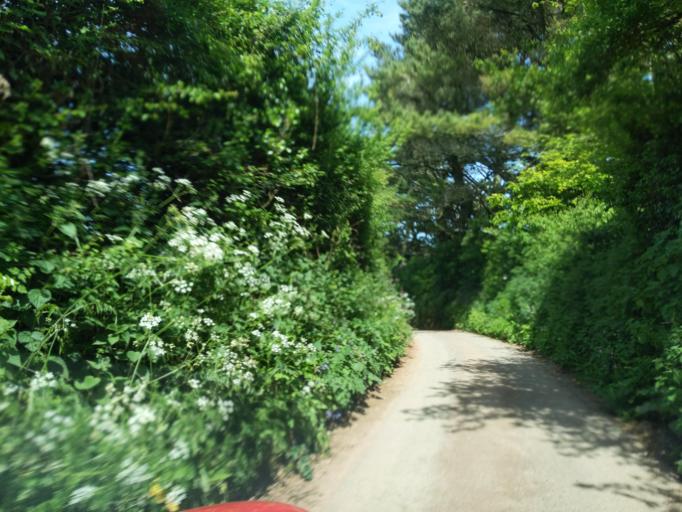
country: GB
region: England
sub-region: Borough of Torbay
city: Brixham
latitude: 50.3633
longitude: -3.5305
